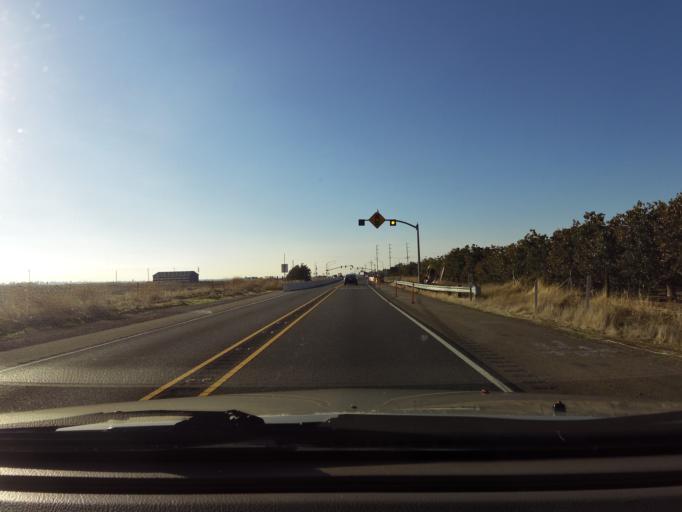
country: US
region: California
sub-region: Madera County
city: Bonadelle Ranchos-Madera Ranchos
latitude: 36.9261
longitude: -119.7940
